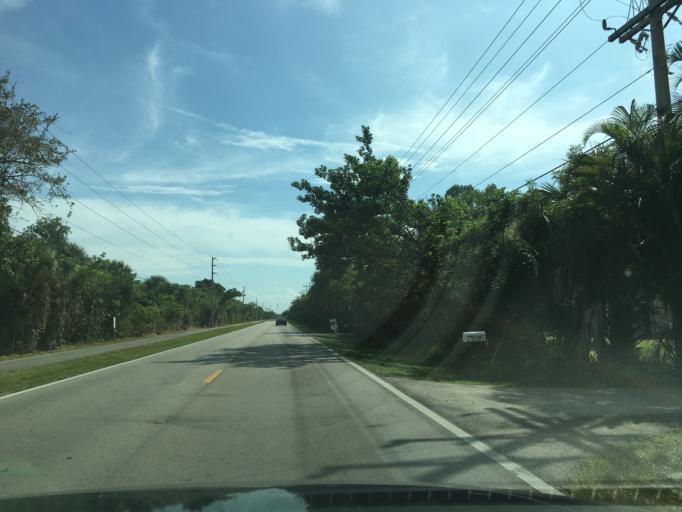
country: US
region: Florida
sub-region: Lee County
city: Saint James City
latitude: 26.4493
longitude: -82.1230
